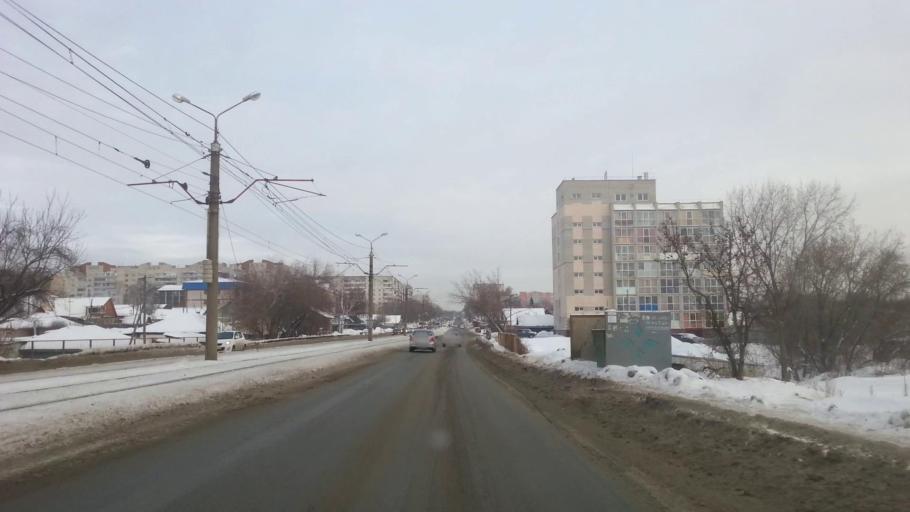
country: RU
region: Altai Krai
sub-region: Gorod Barnaulskiy
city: Barnaul
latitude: 53.3670
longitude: 83.7336
